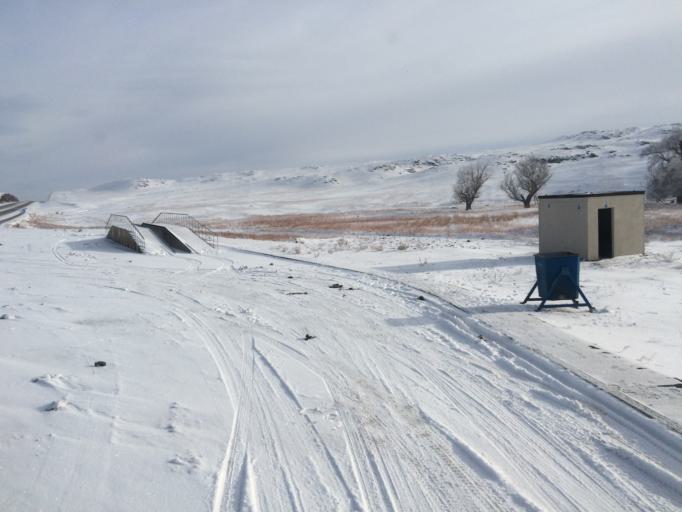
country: KZ
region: Zhambyl
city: Georgiyevka
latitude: 43.4328
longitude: 74.9345
